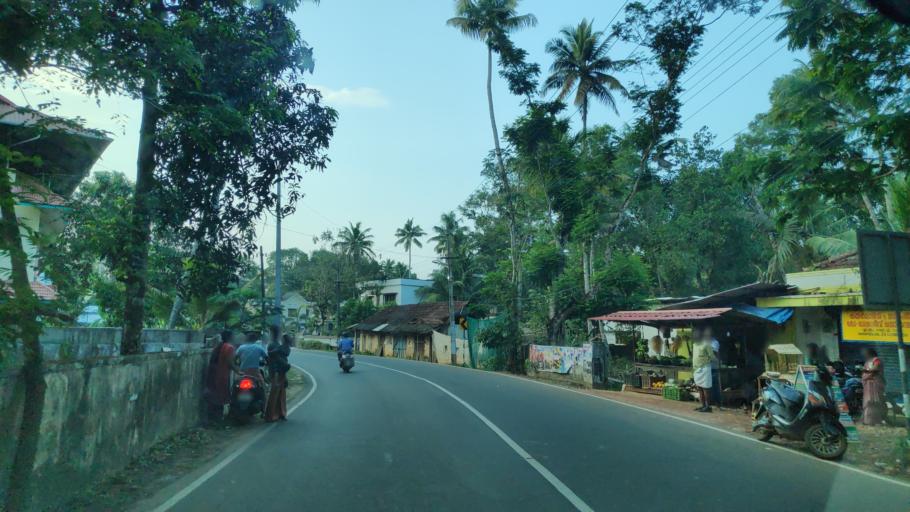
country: IN
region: Kerala
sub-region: Alappuzha
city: Shertallai
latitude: 9.6824
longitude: 76.3627
